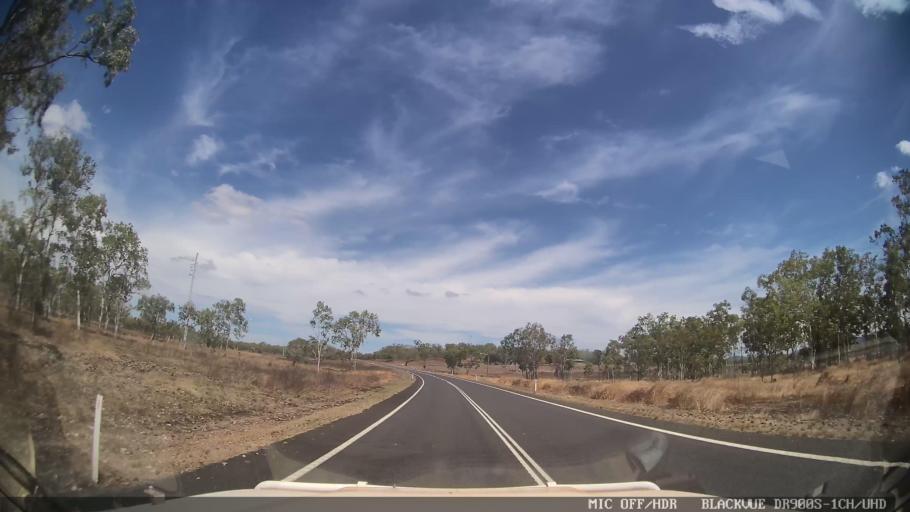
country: AU
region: Queensland
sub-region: Cook
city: Cooktown
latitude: -15.7938
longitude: 144.9283
